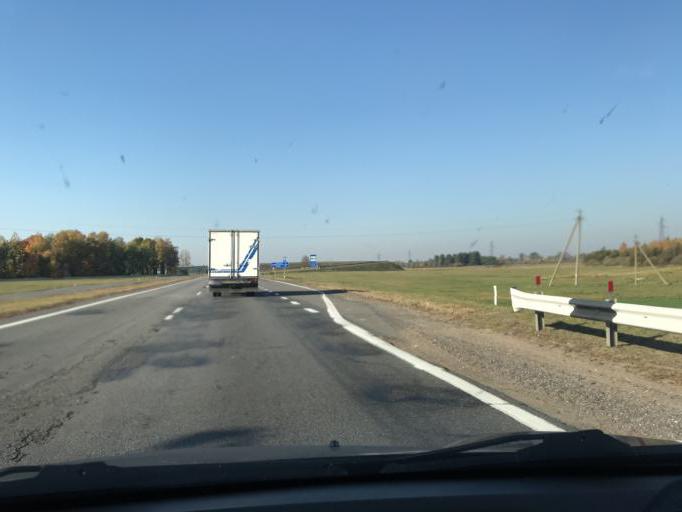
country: BY
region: Minsk
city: Dukora
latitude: 53.6574
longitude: 27.9551
